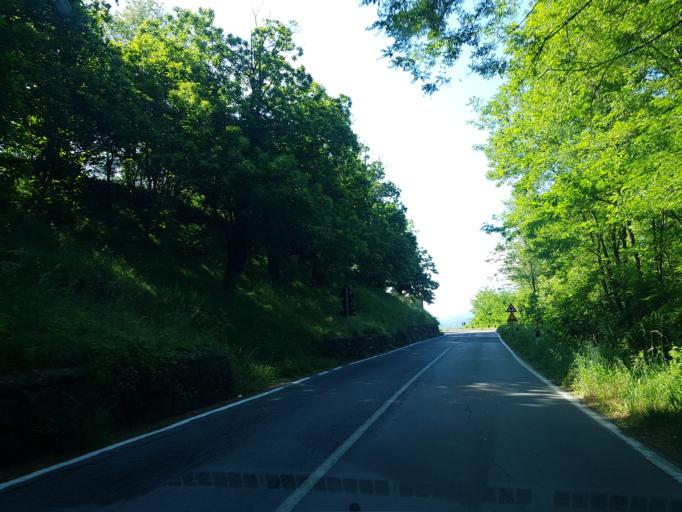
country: IT
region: Tuscany
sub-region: Provincia di Lucca
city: San Romano
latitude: 44.1726
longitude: 10.3374
